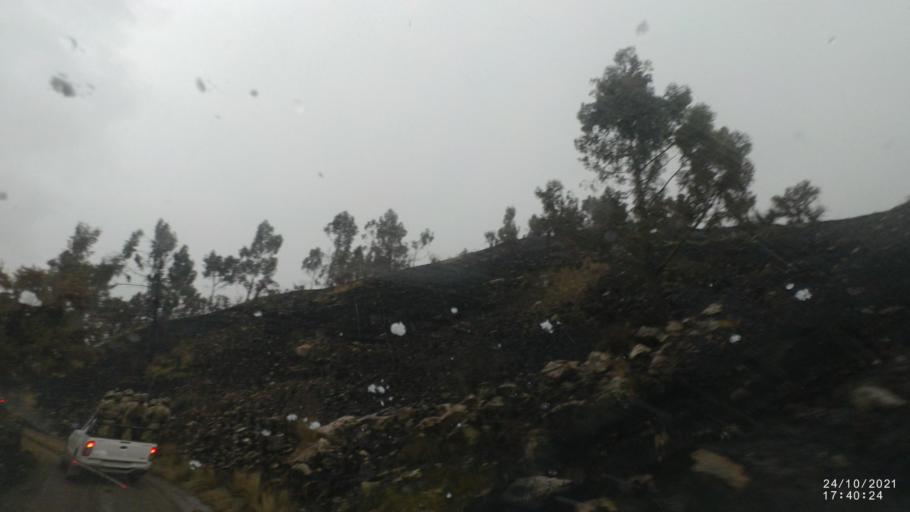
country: BO
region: Cochabamba
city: Cochabamba
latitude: -17.3161
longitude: -66.1301
